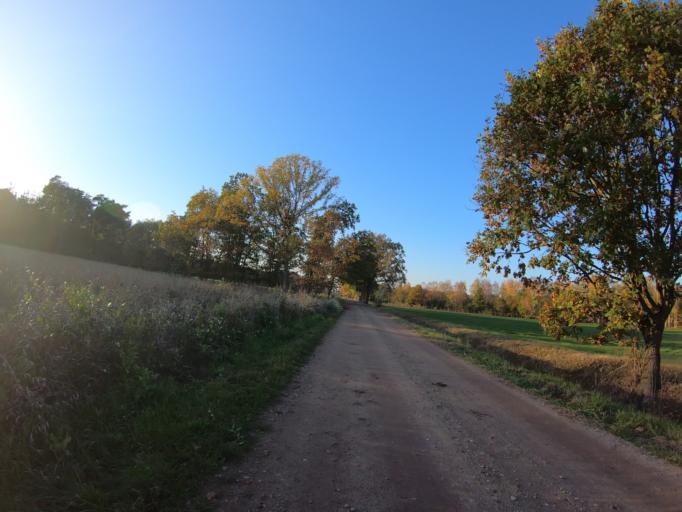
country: DE
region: Lower Saxony
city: Wagenhoff
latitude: 52.5116
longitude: 10.5100
